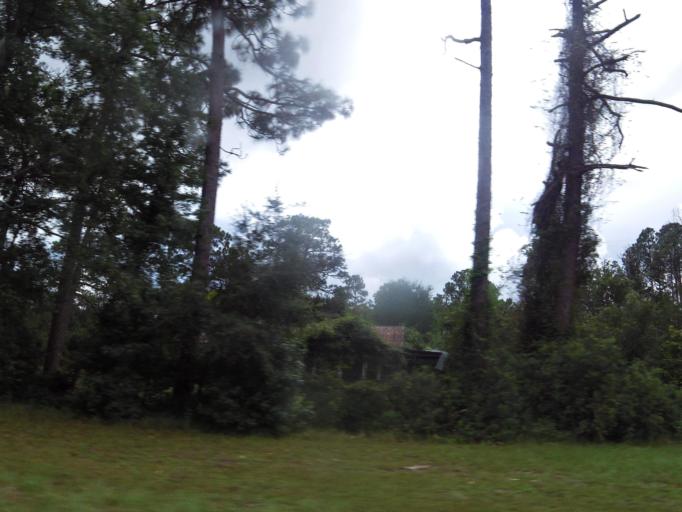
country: US
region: Florida
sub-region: Baker County
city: Macclenny
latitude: 30.5175
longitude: -82.0965
